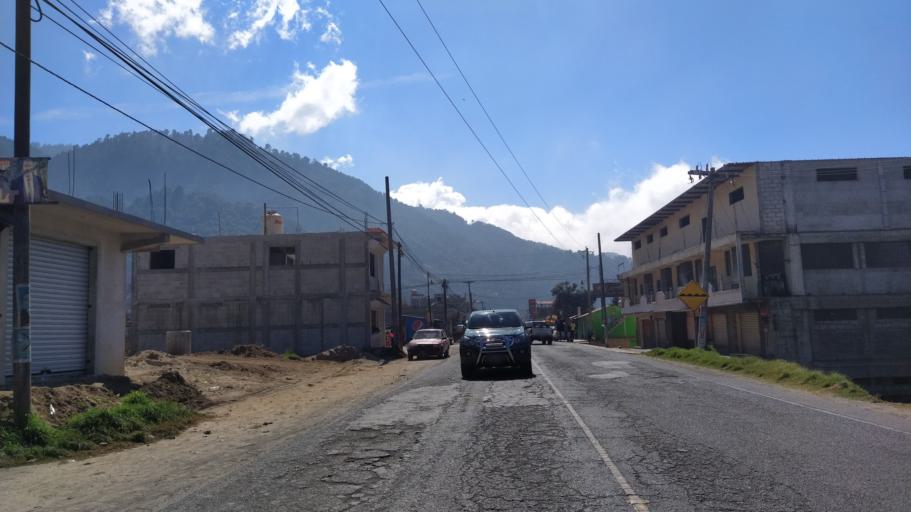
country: GT
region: Quetzaltenango
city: Cantel
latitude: 14.8061
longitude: -91.4481
